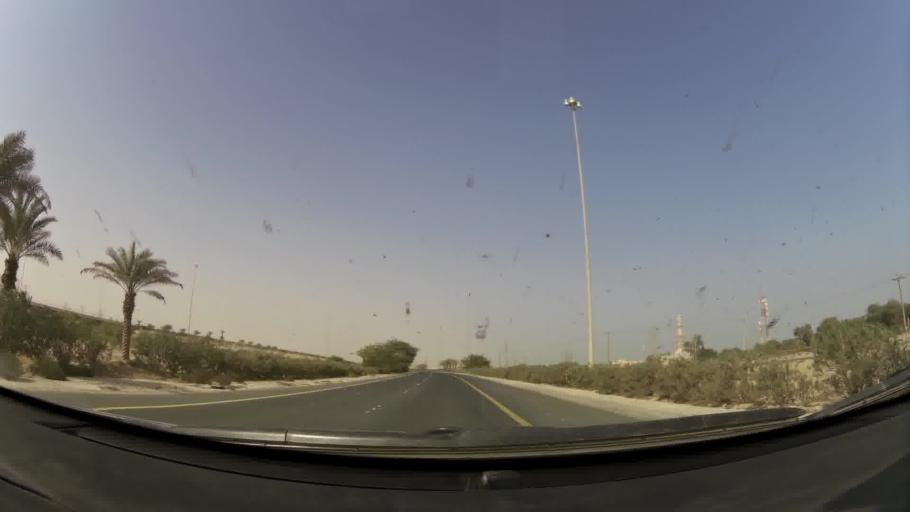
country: KW
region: Al Ahmadi
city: Al Fahahil
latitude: 28.9200
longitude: 48.2068
